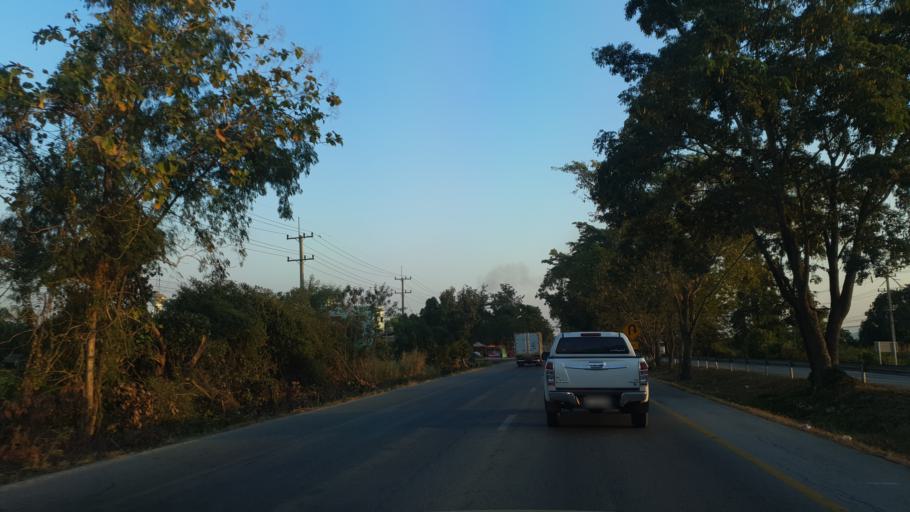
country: TH
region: Nakhon Sawan
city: Banphot Phisai
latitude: 15.8925
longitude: 99.8993
